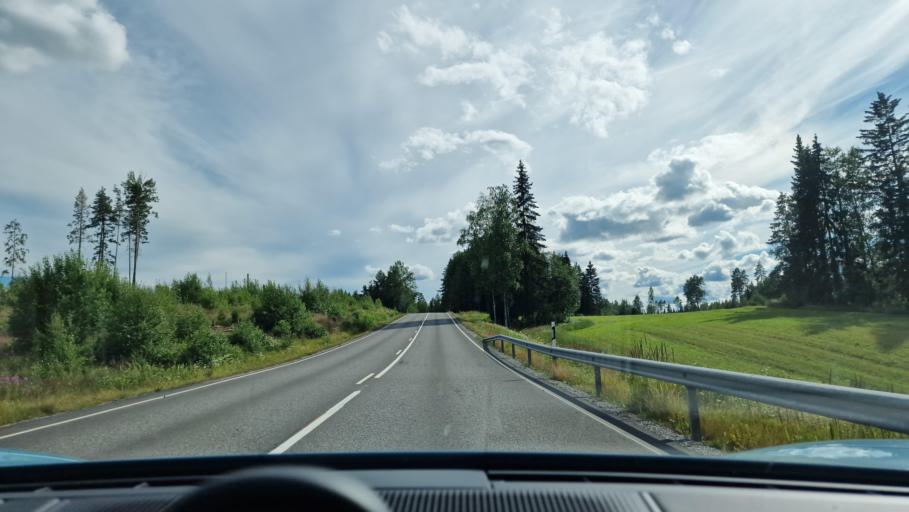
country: FI
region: Pirkanmaa
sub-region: Tampere
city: Sahalahti
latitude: 61.5781
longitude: 24.3021
